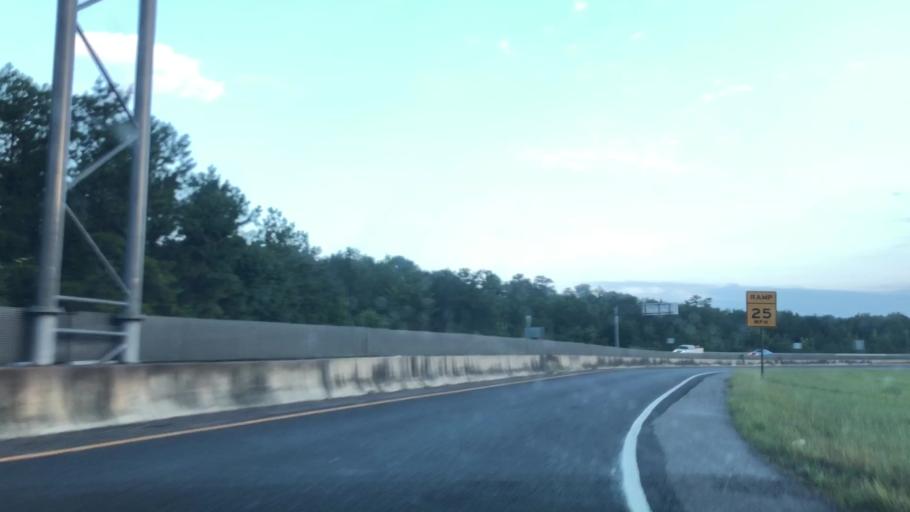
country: US
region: Alabama
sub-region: Shelby County
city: Indian Springs Village
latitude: 33.3539
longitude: -86.7811
